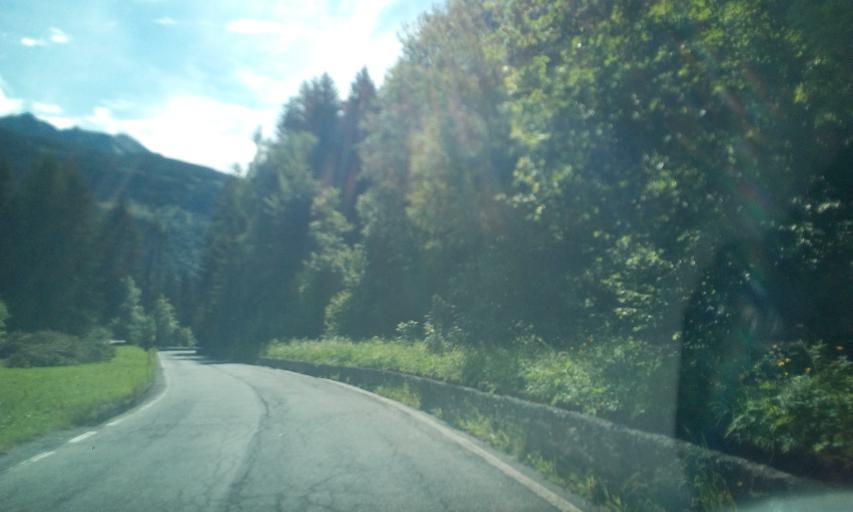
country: IT
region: Aosta Valley
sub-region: Valle d'Aosta
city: Brusson
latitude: 45.7575
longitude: 7.7184
